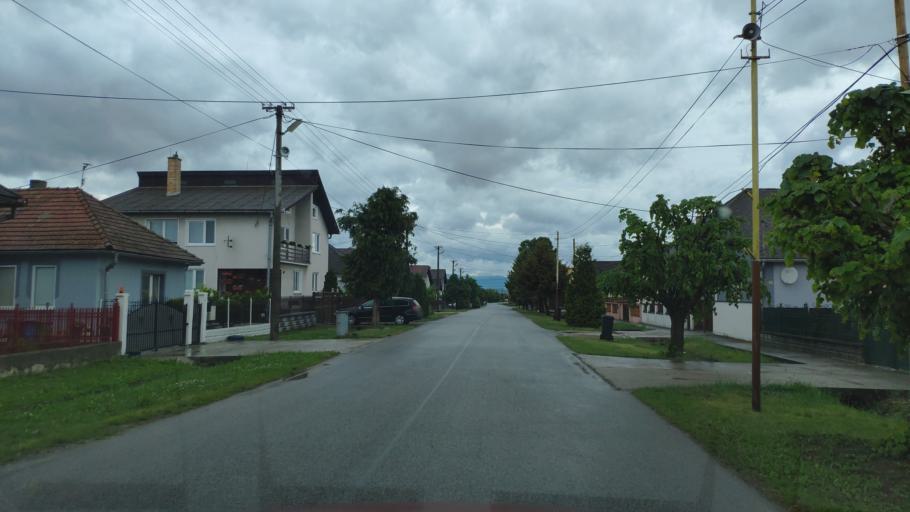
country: SK
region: Kosicky
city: Moldava nad Bodvou
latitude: 48.5354
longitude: 21.1096
